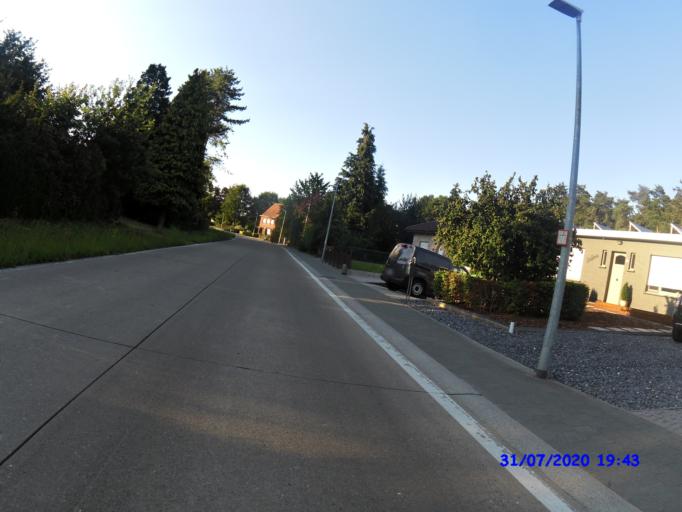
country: BE
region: Flanders
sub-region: Provincie Antwerpen
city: Kasterlee
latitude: 51.2362
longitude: 4.9589
